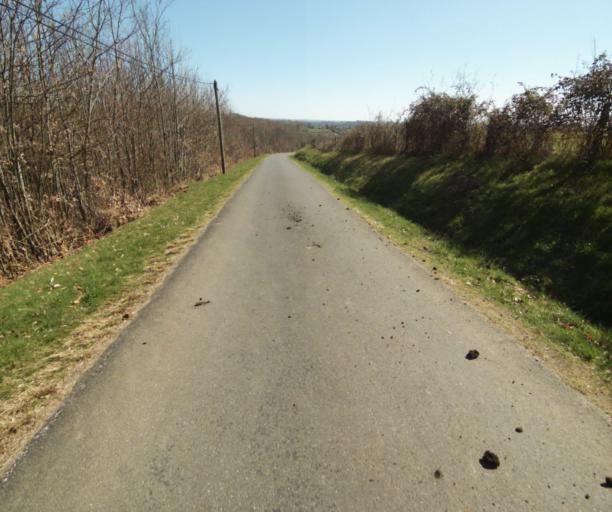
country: FR
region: Limousin
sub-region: Departement de la Correze
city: Saint-Clement
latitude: 45.3314
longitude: 1.6959
